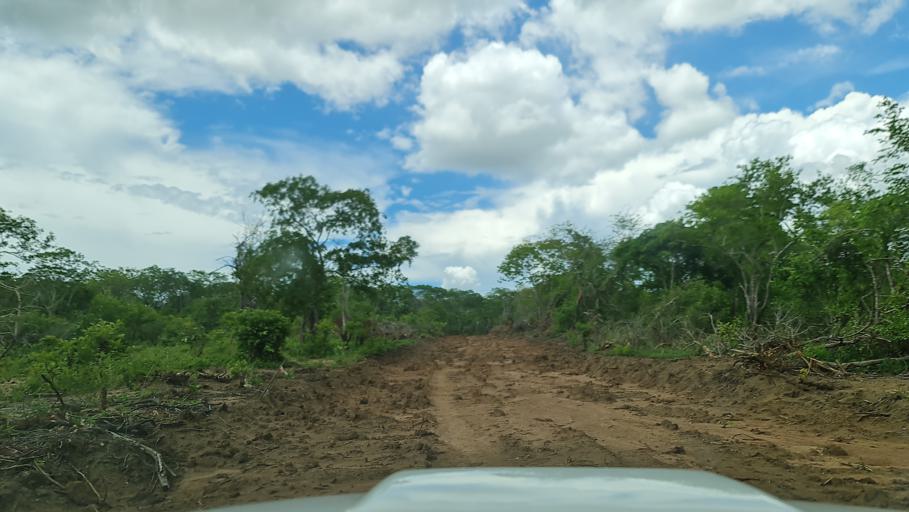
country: MZ
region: Nampula
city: Ilha de Mocambique
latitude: -15.5073
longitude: 40.1893
